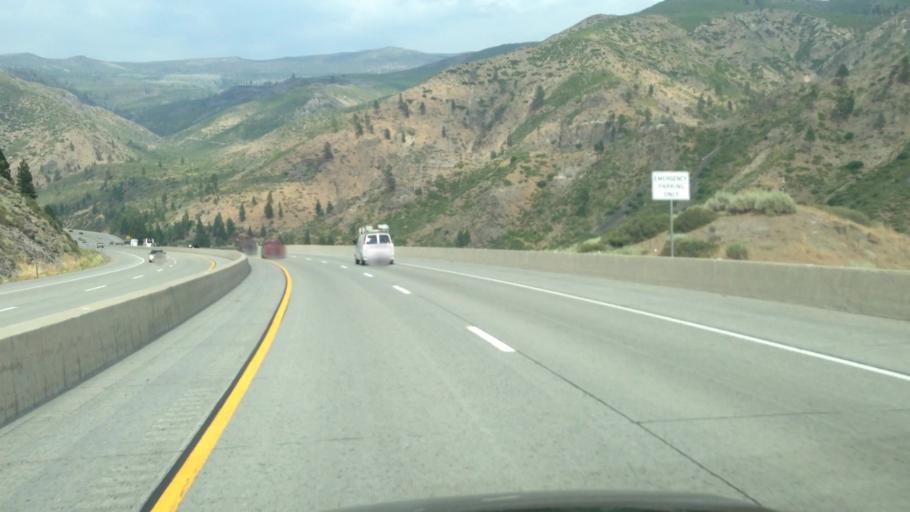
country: US
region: California
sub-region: Placer County
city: Tahoe Vista
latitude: 39.3704
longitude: -120.0416
